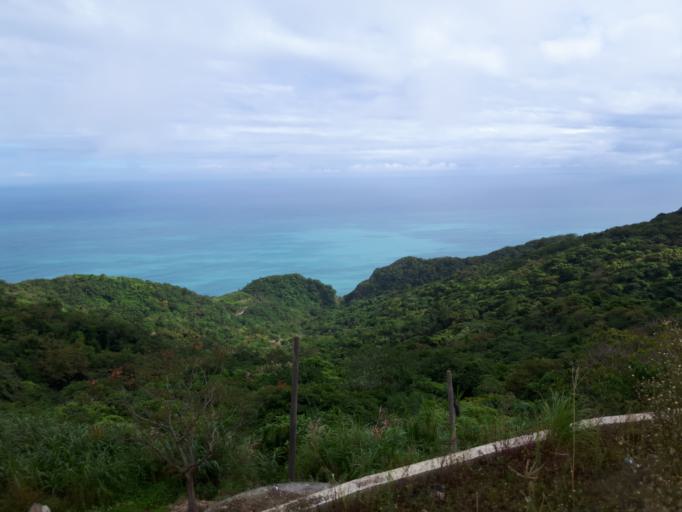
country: TW
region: Taiwan
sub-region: Hualien
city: Hualian
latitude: 23.8908
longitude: 121.5904
